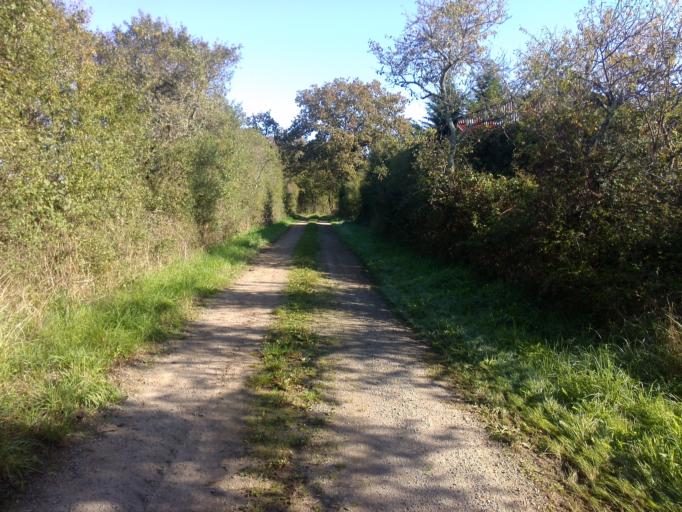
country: FR
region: Pays de la Loire
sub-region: Departement de la Loire-Atlantique
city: Chemere
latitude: 47.1113
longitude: -1.9026
